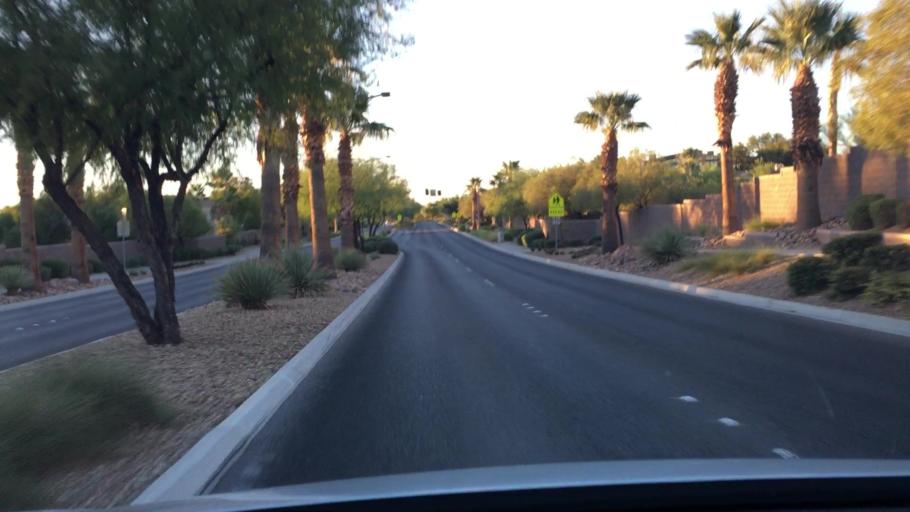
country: US
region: Nevada
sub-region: Clark County
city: Summerlin South
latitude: 36.1295
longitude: -115.3421
